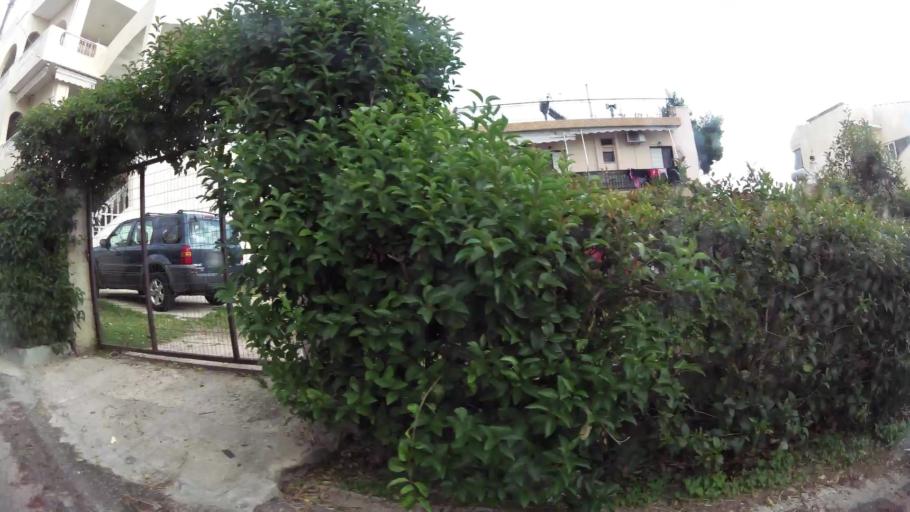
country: GR
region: Attica
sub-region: Nomarchia Dytikis Attikis
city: Zefyri
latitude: 38.0568
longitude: 23.7220
